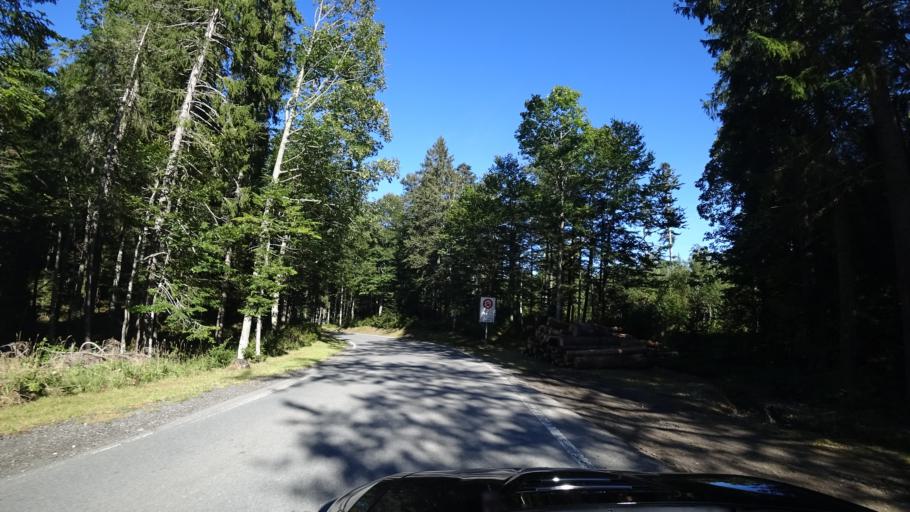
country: CH
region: Obwalden
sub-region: Obwalden
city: Lungern
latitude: 46.8261
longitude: 8.1144
